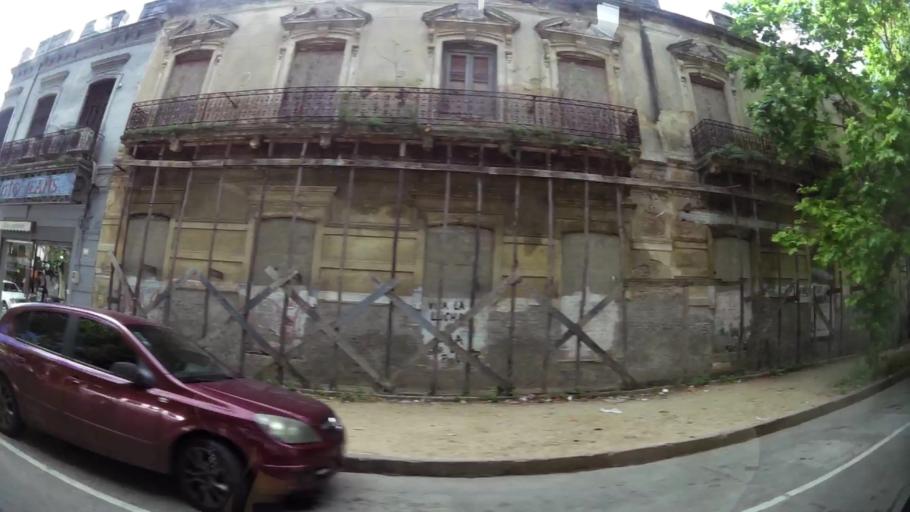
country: UY
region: Montevideo
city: Montevideo
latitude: -34.8830
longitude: -56.1781
